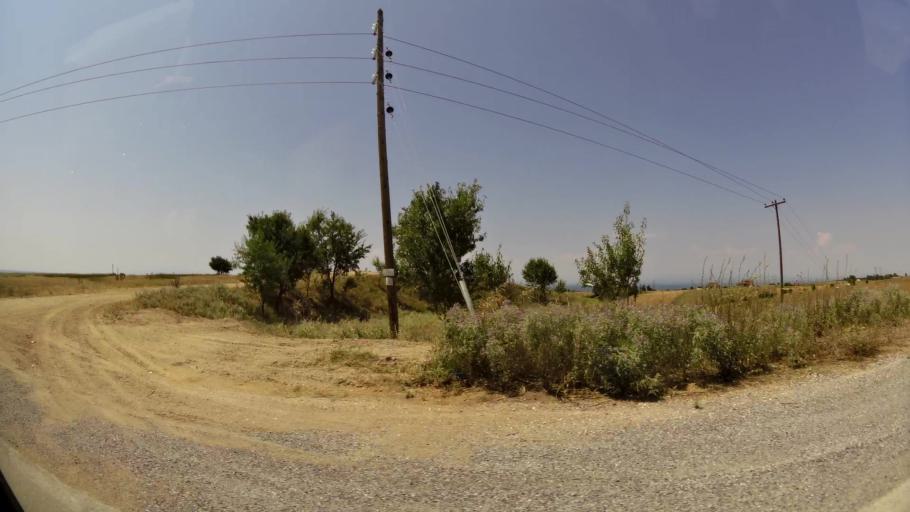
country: GR
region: Central Macedonia
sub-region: Nomos Thessalonikis
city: Neoi Epivates
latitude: 40.4663
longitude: 22.9016
